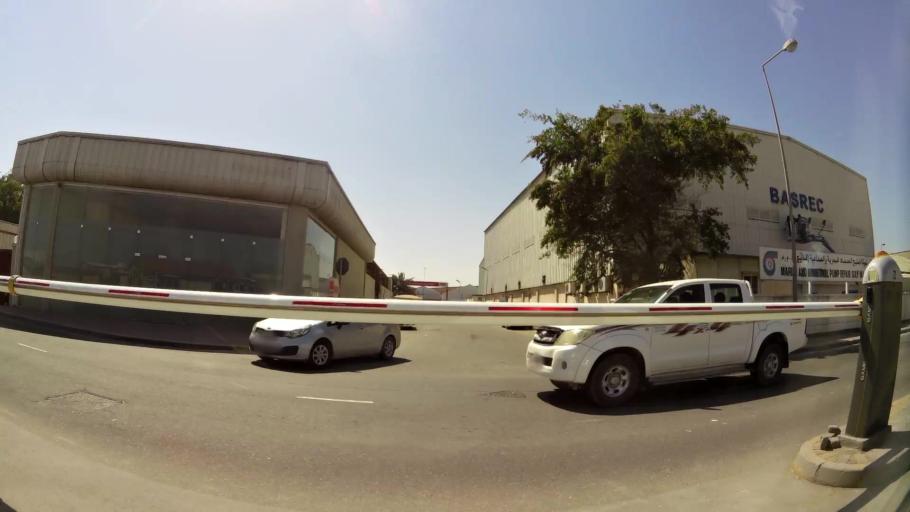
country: BH
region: Manama
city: Manama
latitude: 26.2016
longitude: 50.6031
